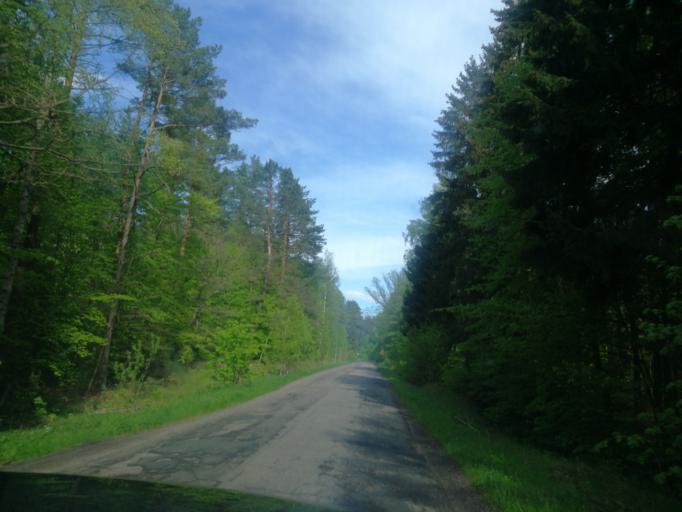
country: PL
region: Warmian-Masurian Voivodeship
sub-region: Powiat ostrodzki
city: Milomlyn
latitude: 53.6915
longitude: 19.6991
